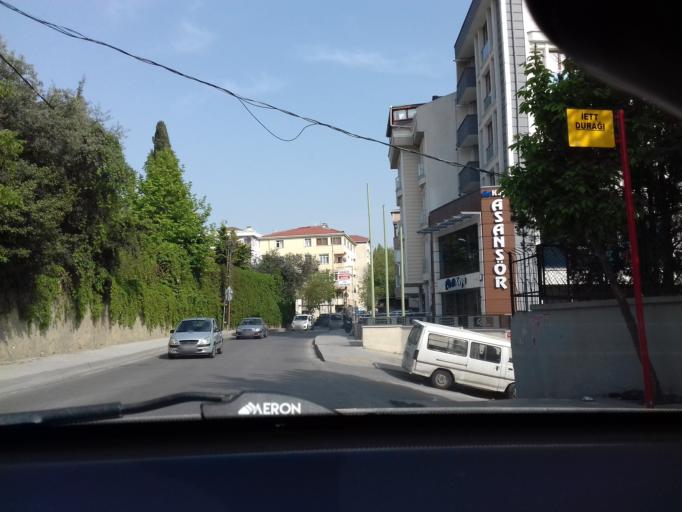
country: TR
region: Istanbul
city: Pendik
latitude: 40.9133
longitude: 29.2265
